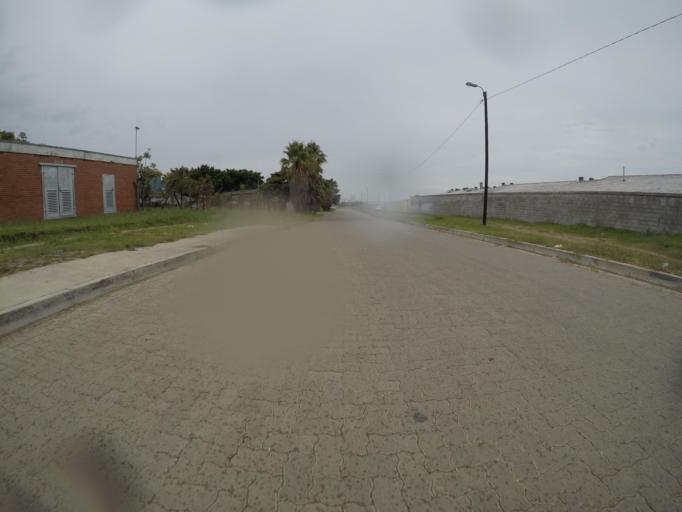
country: ZA
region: Eastern Cape
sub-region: Buffalo City Metropolitan Municipality
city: East London
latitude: -32.9910
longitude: 27.8303
